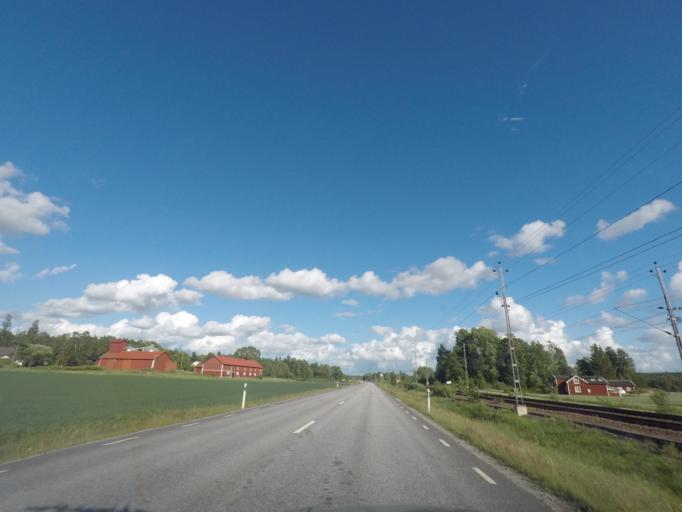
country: SE
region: Vaestmanland
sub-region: Arboga Kommun
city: Arboga
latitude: 59.4065
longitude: 15.8006
